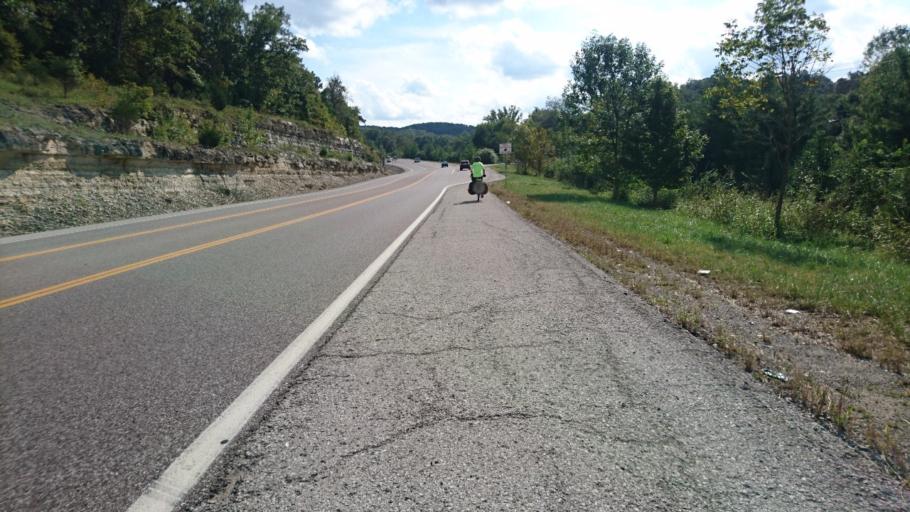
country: US
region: Missouri
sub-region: Saint Louis County
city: Eureka
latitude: 38.5422
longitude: -90.6307
